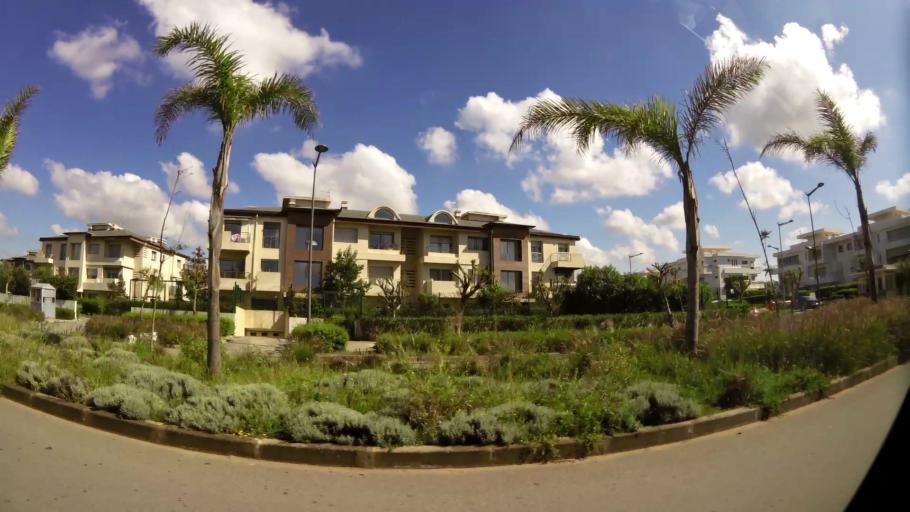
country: MA
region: Grand Casablanca
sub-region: Nouaceur
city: Bouskoura
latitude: 33.4728
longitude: -7.6120
